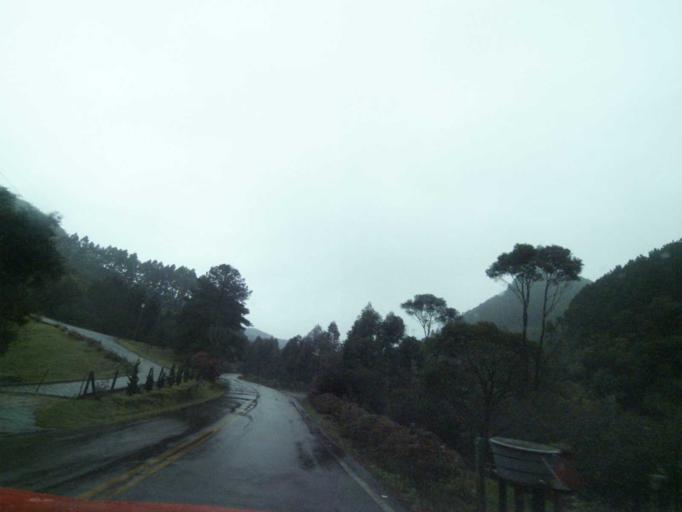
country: BR
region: Santa Catarina
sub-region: Anitapolis
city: Anitapolis
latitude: -27.8046
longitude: -49.0465
